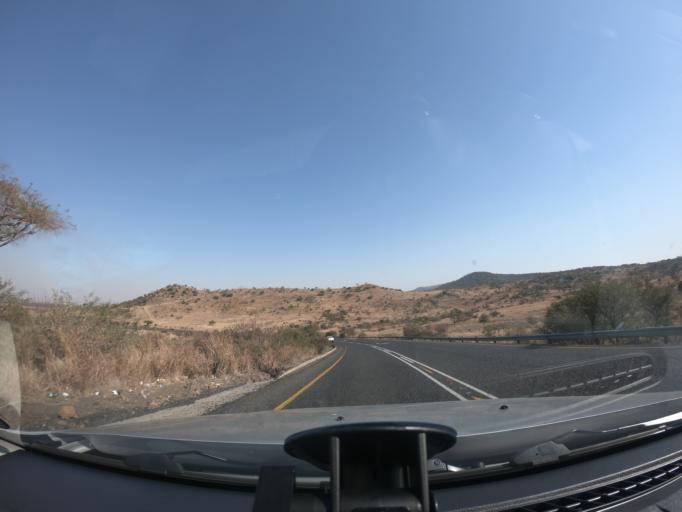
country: ZA
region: KwaZulu-Natal
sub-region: uThukela District Municipality
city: Ladysmith
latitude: -28.6719
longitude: 29.8314
